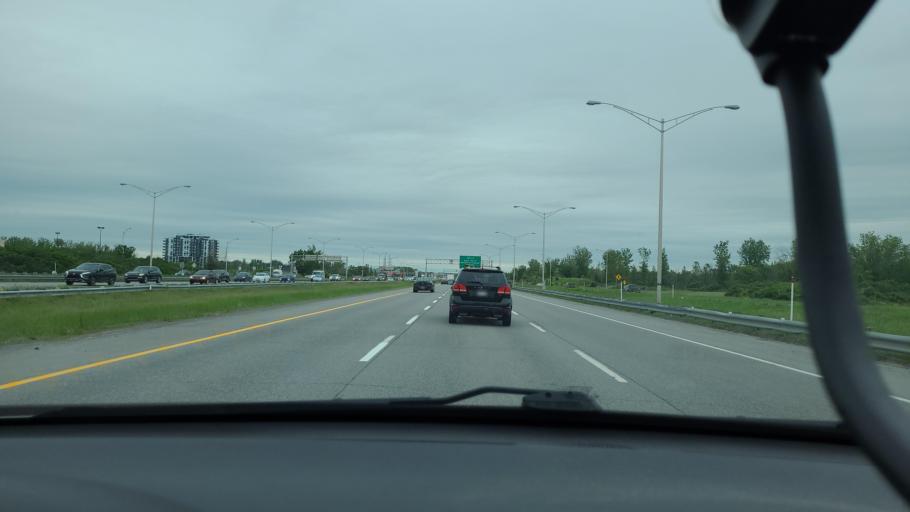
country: CA
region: Quebec
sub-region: Laval
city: Laval
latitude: 45.6053
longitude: -73.6969
